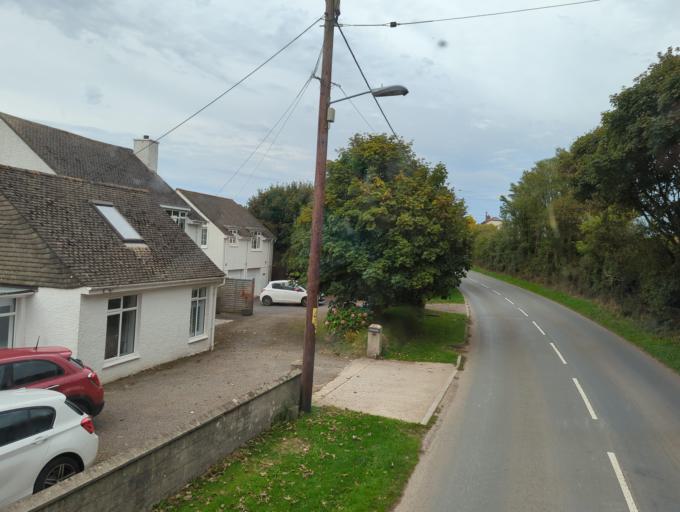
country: GB
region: England
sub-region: Cornwall
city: Wadebridge
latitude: 50.5808
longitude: -4.7917
